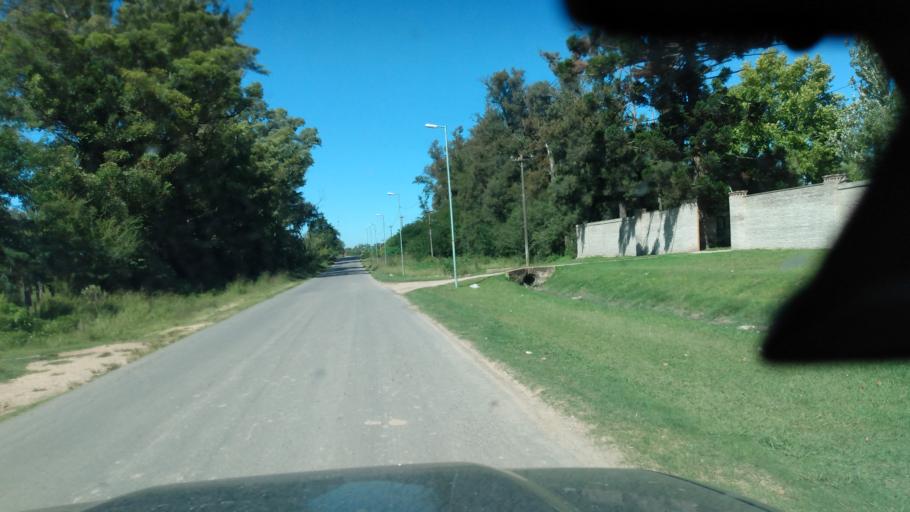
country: AR
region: Buenos Aires
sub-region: Partido de Lujan
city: Lujan
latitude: -34.5725
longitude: -59.1298
